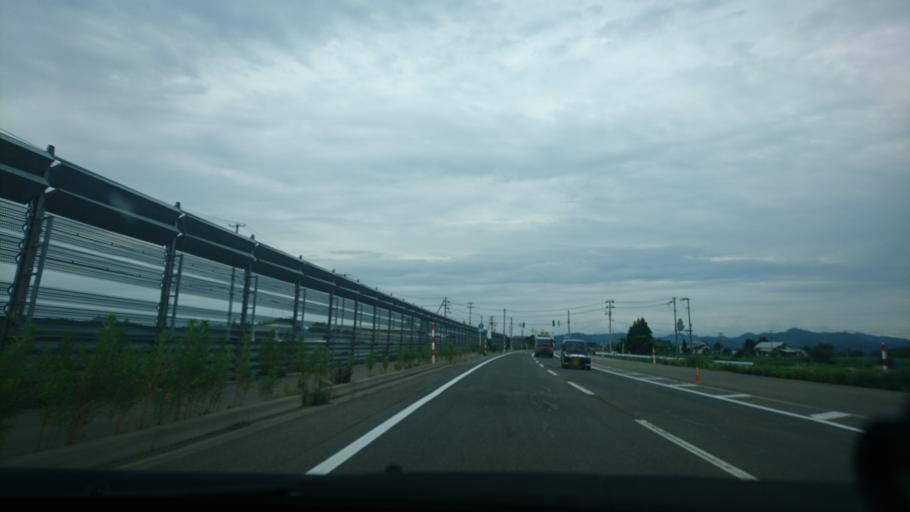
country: JP
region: Akita
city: Omagari
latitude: 39.5136
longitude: 140.3793
